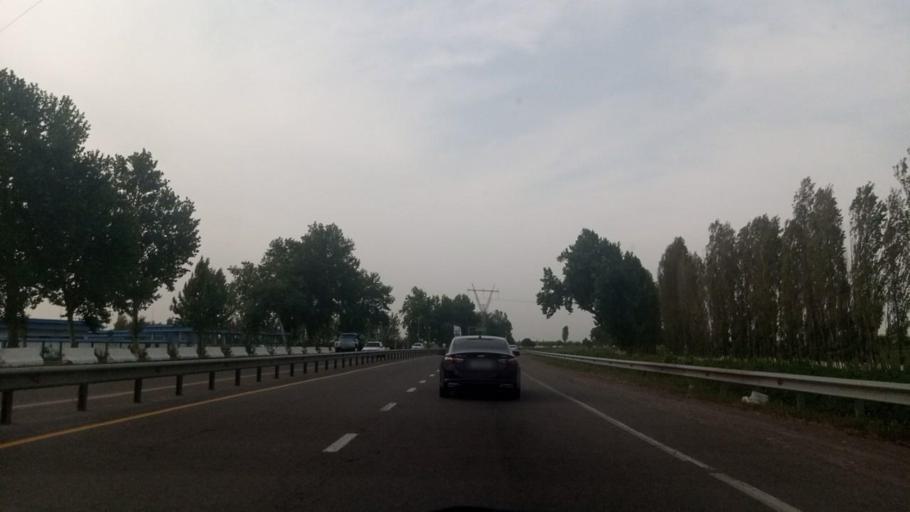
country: UZ
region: Toshkent Shahri
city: Bektemir
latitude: 41.1850
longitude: 69.4045
